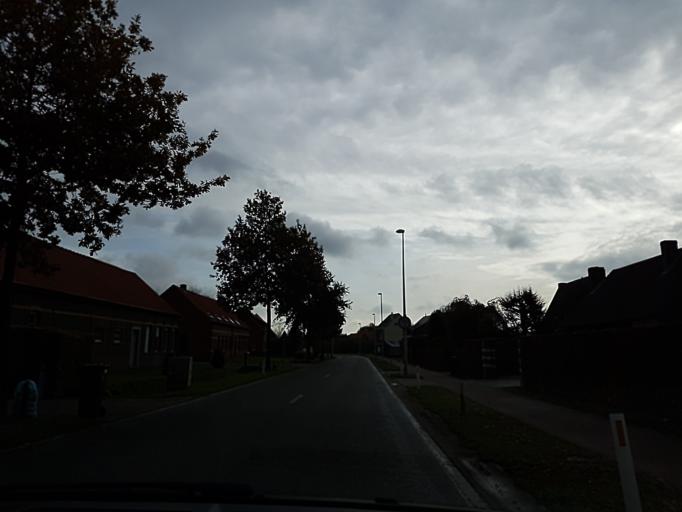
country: BE
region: Flanders
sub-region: Provincie Antwerpen
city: Lier
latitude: 51.1566
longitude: 4.5521
